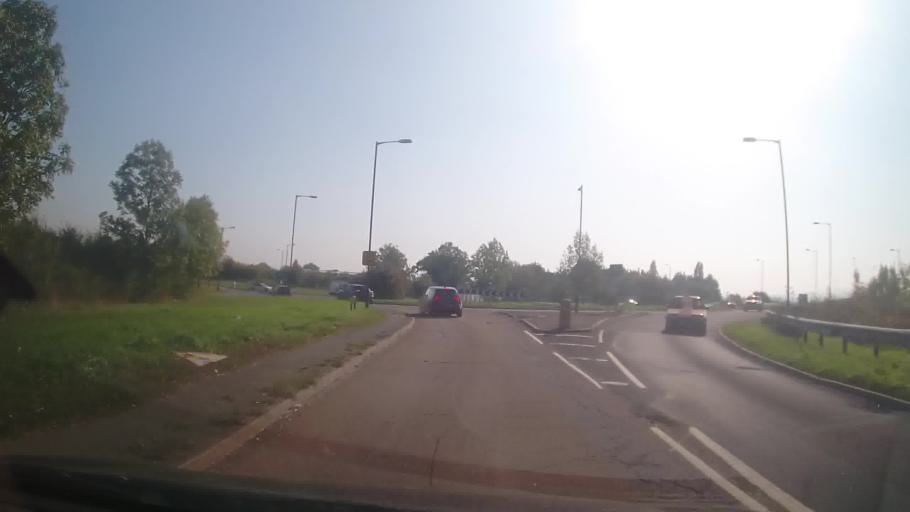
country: GB
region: England
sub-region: Worcestershire
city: Pershore
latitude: 52.1313
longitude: -2.0660
